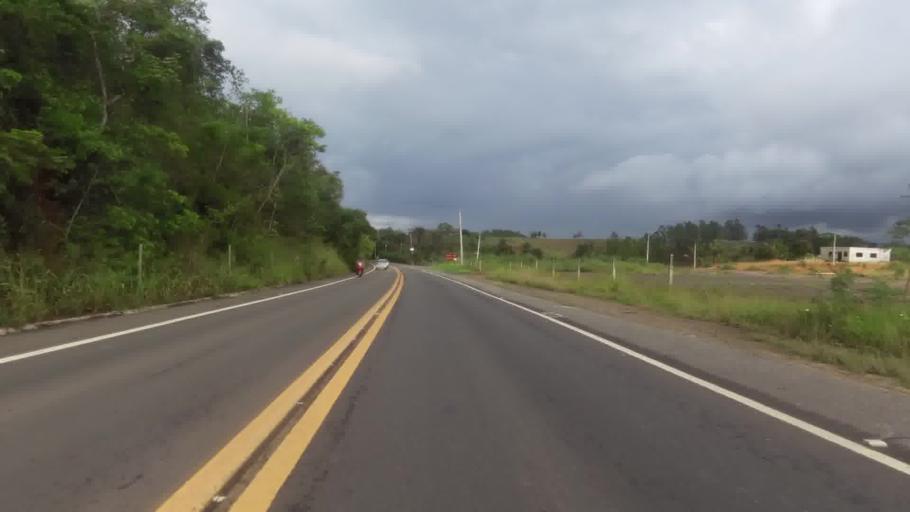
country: BR
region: Espirito Santo
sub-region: Piuma
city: Piuma
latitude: -20.8066
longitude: -40.6769
